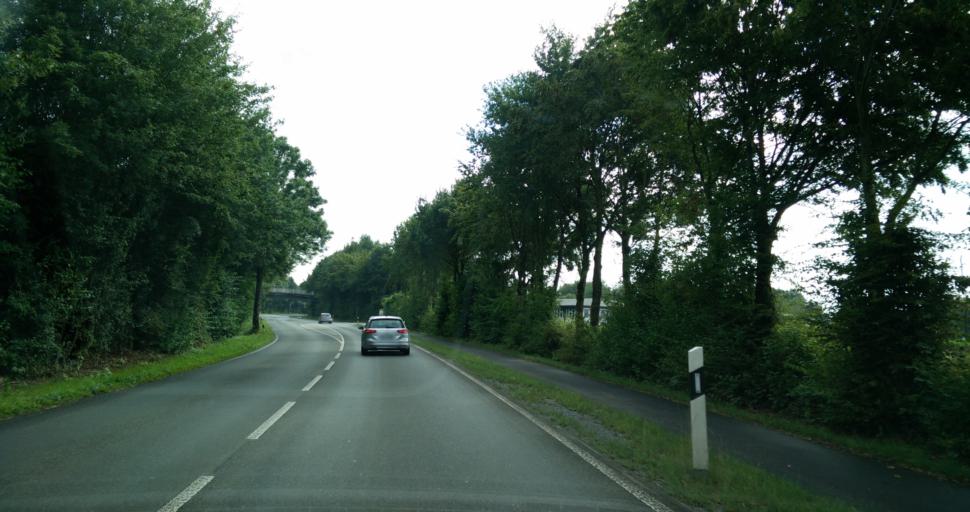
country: DE
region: North Rhine-Westphalia
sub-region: Regierungsbezirk Dusseldorf
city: Mettmann
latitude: 51.2394
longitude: 7.0048
